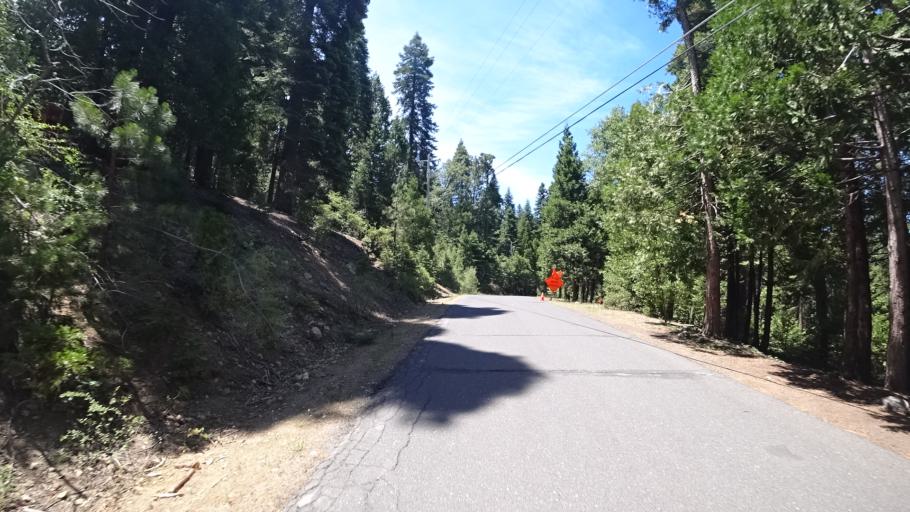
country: US
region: California
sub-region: Calaveras County
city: Arnold
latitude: 38.3167
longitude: -120.2549
